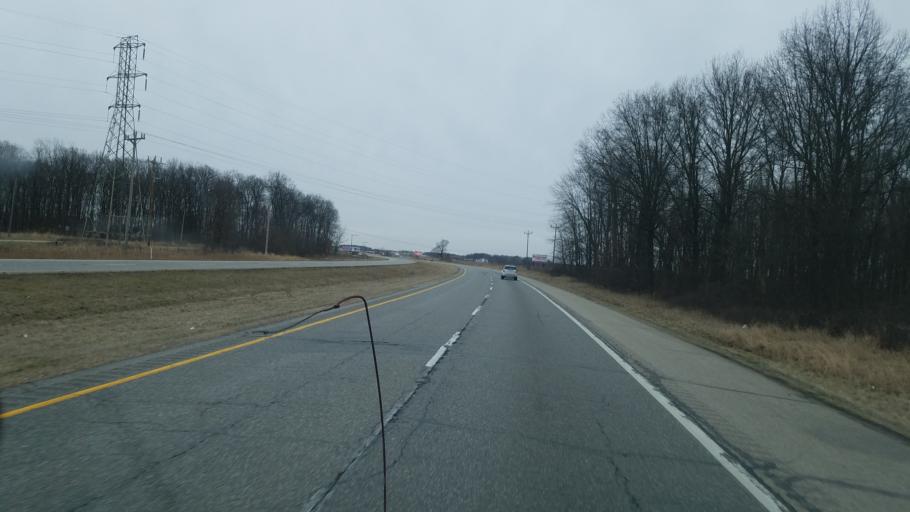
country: US
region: Indiana
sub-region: Marshall County
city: Plymouth
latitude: 41.3618
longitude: -86.3700
